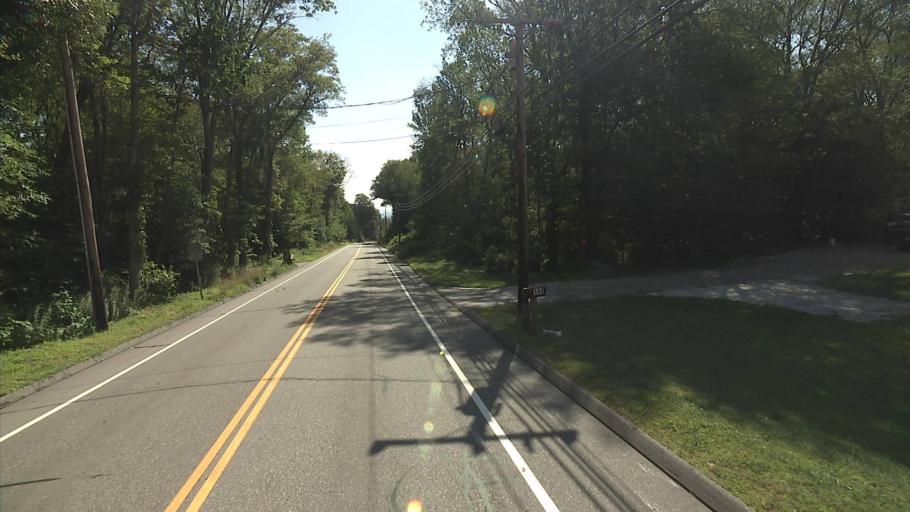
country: US
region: Connecticut
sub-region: Tolland County
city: Crystal Lake
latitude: 41.9762
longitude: -72.3812
